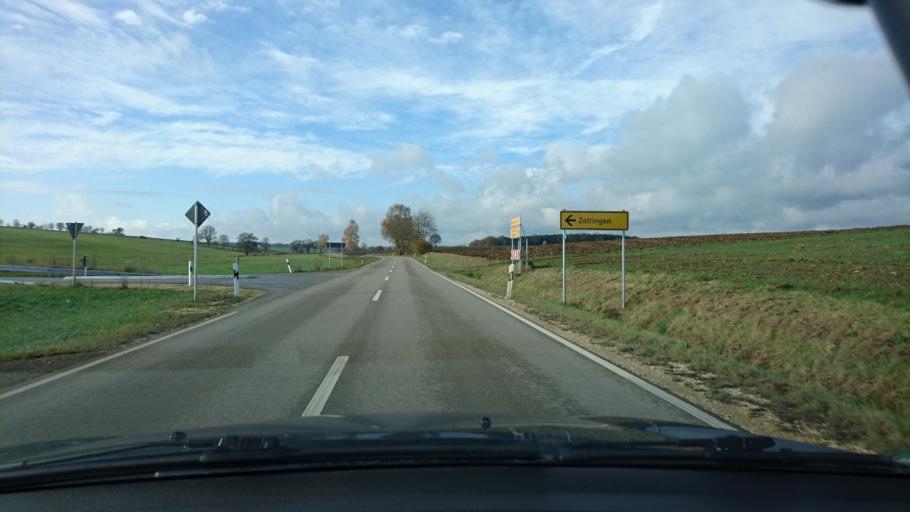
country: DE
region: Bavaria
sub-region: Swabia
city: Amerdingen
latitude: 48.7269
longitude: 10.5188
